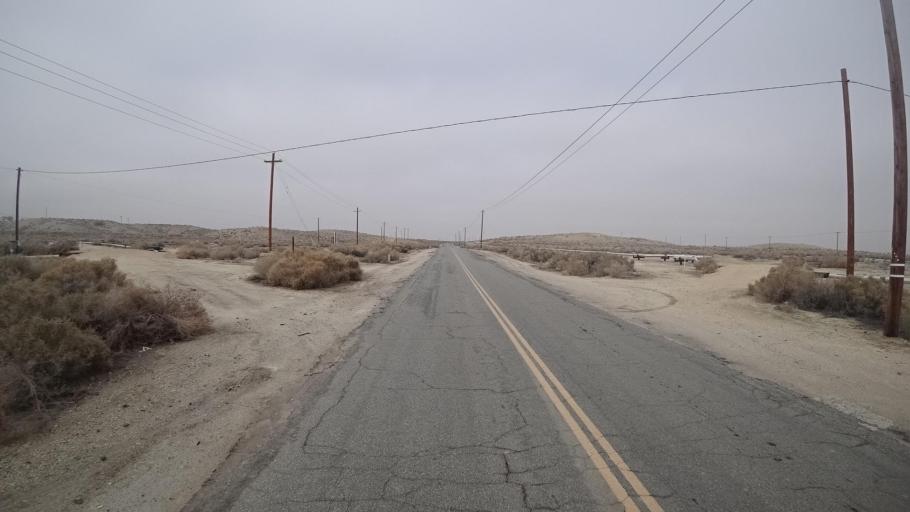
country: US
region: California
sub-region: Kern County
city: Maricopa
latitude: 35.0853
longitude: -119.3987
